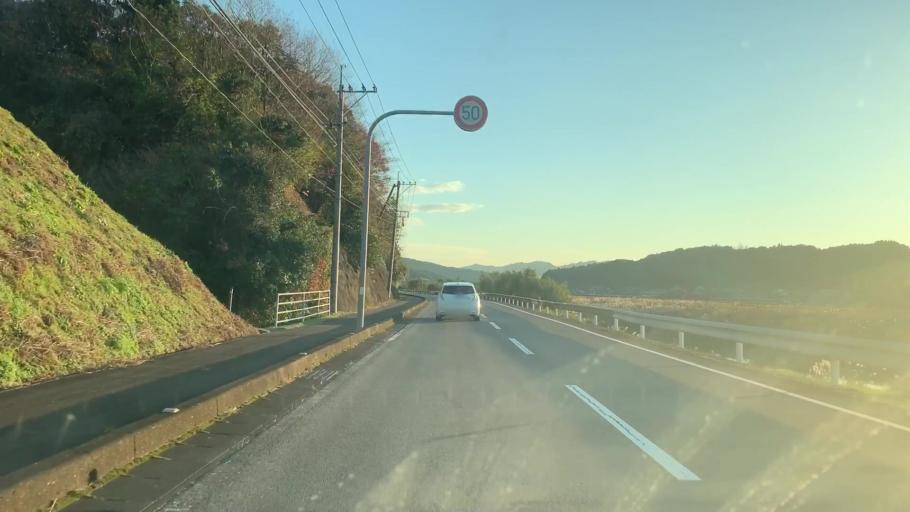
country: JP
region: Saga Prefecture
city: Imaricho-ko
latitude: 33.2772
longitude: 129.9652
